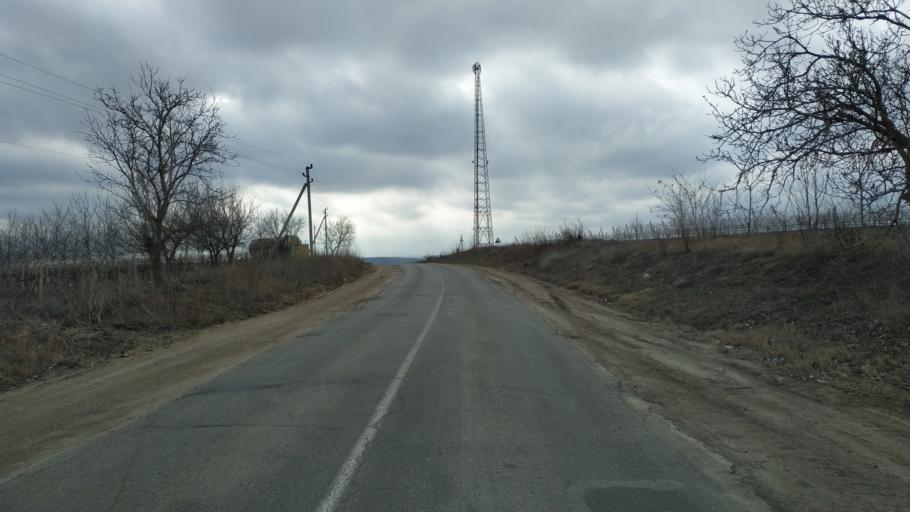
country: MD
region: Laloveni
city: Ialoveni
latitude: 46.8898
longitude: 28.7683
